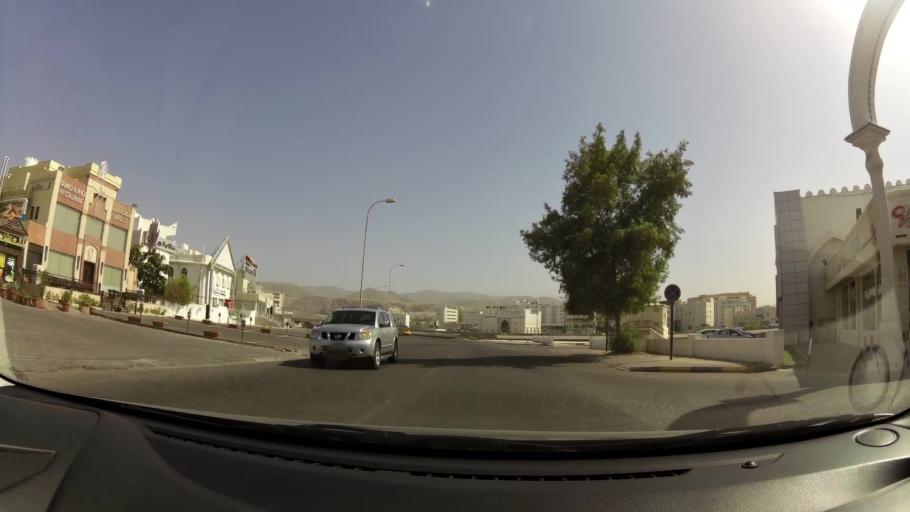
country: OM
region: Muhafazat Masqat
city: Muscat
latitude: 23.6147
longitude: 58.4976
